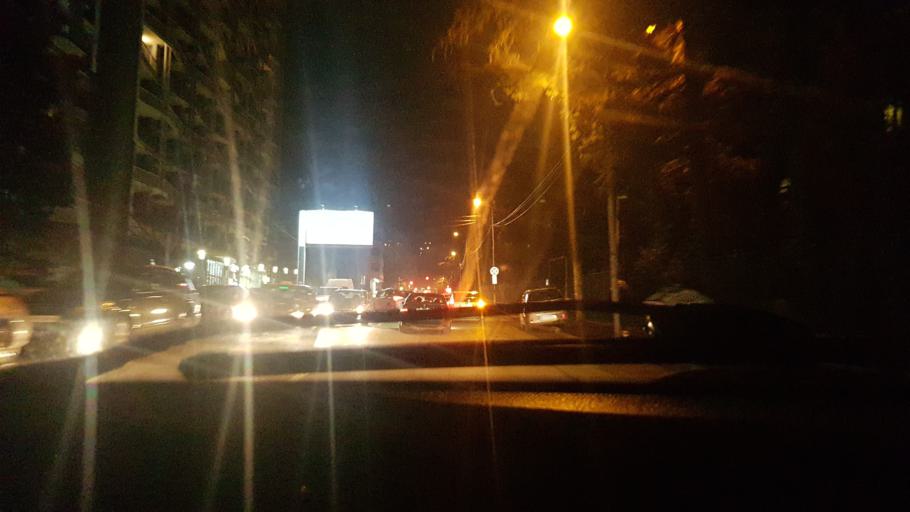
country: GE
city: Tsqnet'i
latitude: 41.7225
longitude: 44.7509
